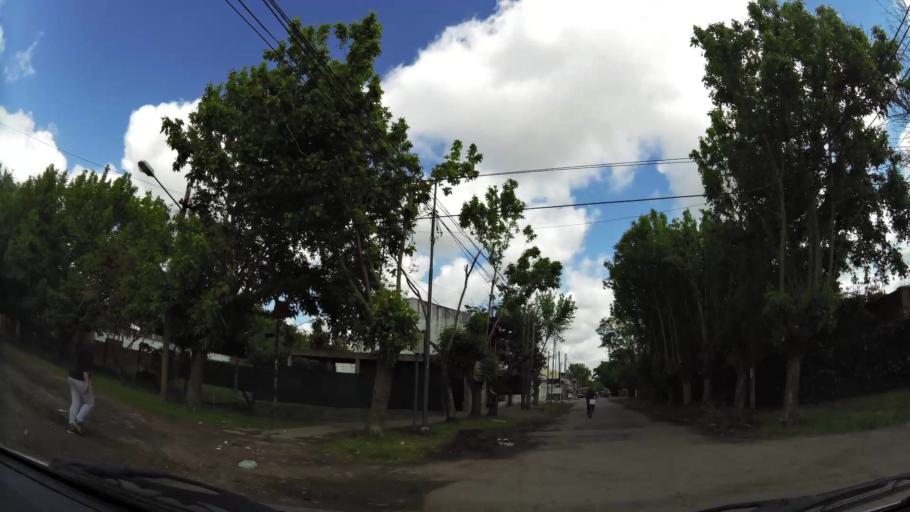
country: AR
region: Buenos Aires
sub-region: Partido de Quilmes
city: Quilmes
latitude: -34.8293
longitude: -58.1860
